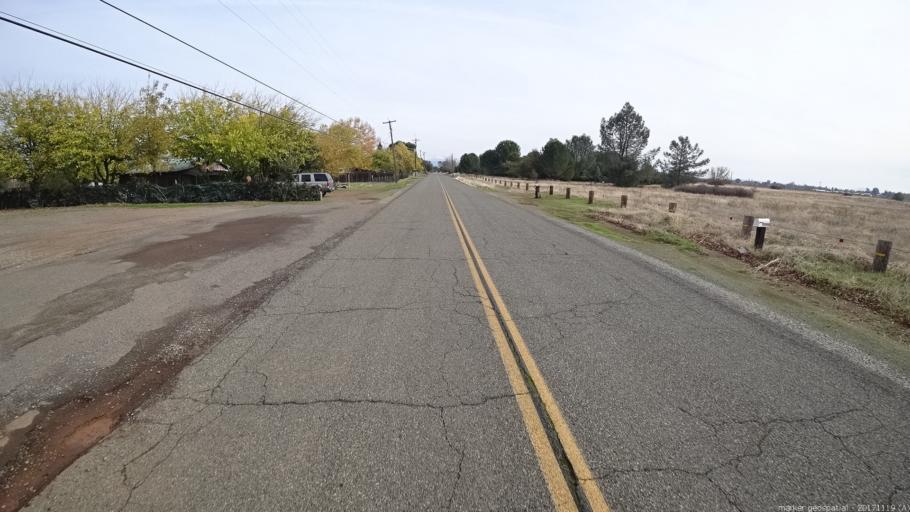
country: US
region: California
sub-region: Shasta County
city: Anderson
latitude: 40.4913
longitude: -122.2817
